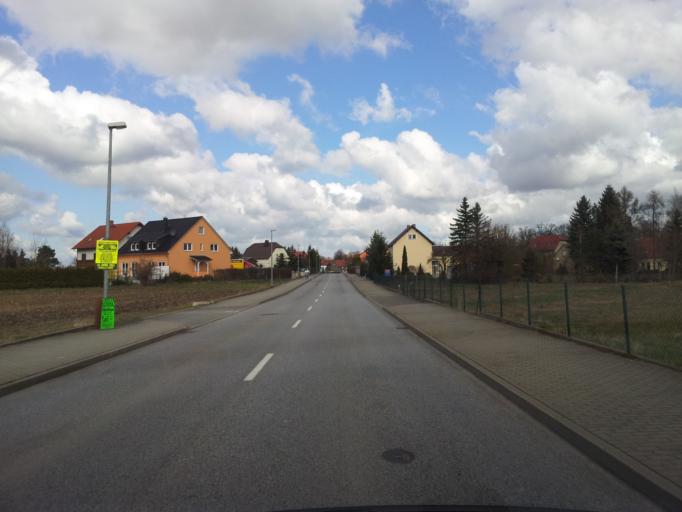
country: DE
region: Saxony
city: Ottendorf-Okrilla
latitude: 51.1806
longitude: 13.8484
